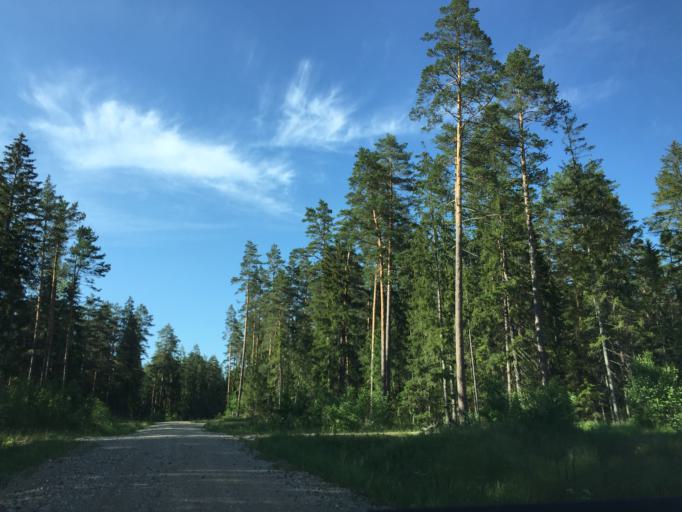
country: LV
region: Tukuma Rajons
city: Tukums
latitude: 57.0356
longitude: 23.2076
